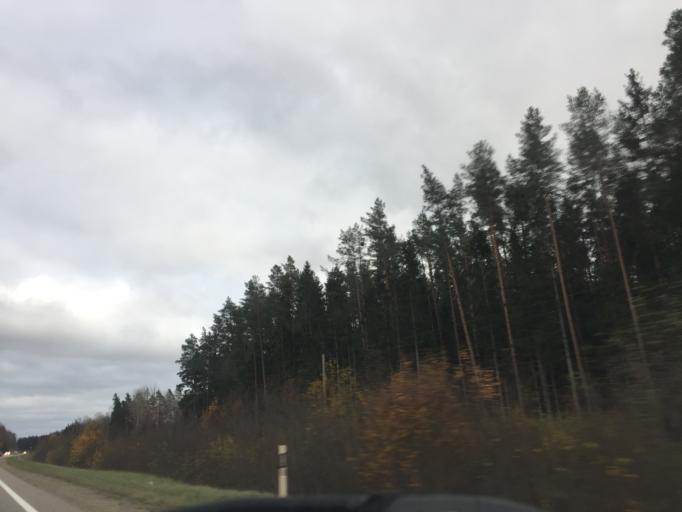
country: LV
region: Saldus Rajons
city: Saldus
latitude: 56.6748
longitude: 22.2609
